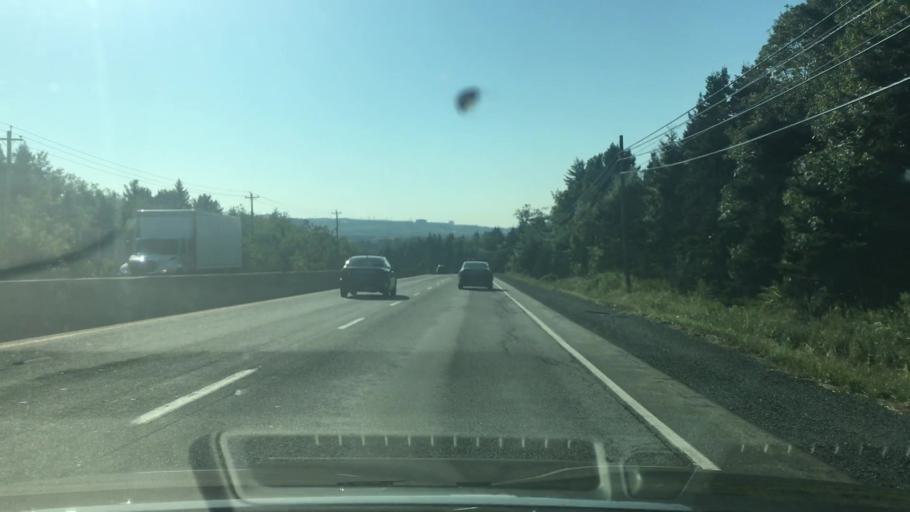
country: CA
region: Nova Scotia
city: Dartmouth
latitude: 44.7106
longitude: -63.6266
